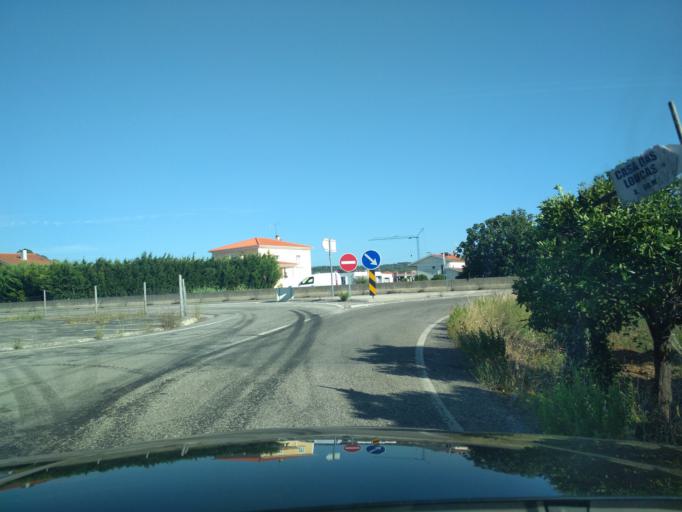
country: PT
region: Coimbra
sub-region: Condeixa-A-Nova
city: Condeixa-a-Nova
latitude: 40.1354
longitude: -8.4712
